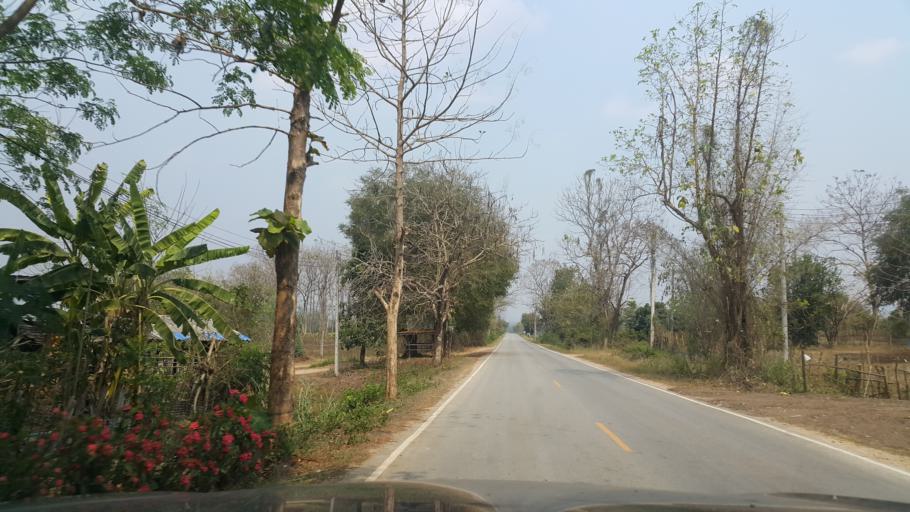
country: TH
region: Lampang
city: Soem Ngam
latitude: 18.0078
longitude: 99.2027
